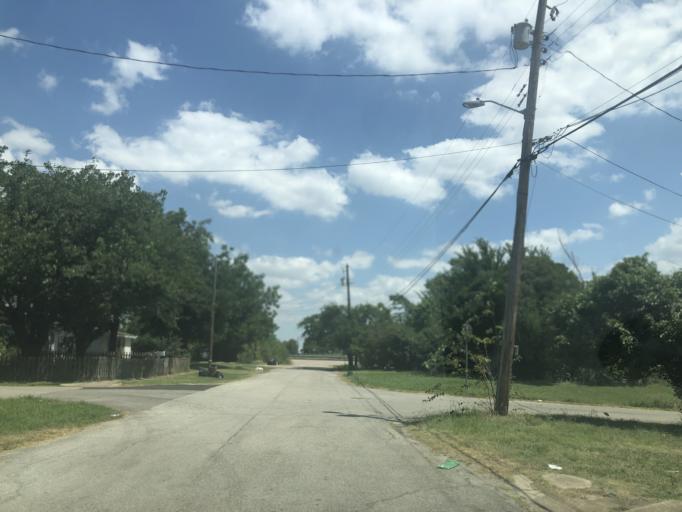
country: US
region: Texas
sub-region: Dallas County
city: Grand Prairie
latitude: 32.7459
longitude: -97.0251
